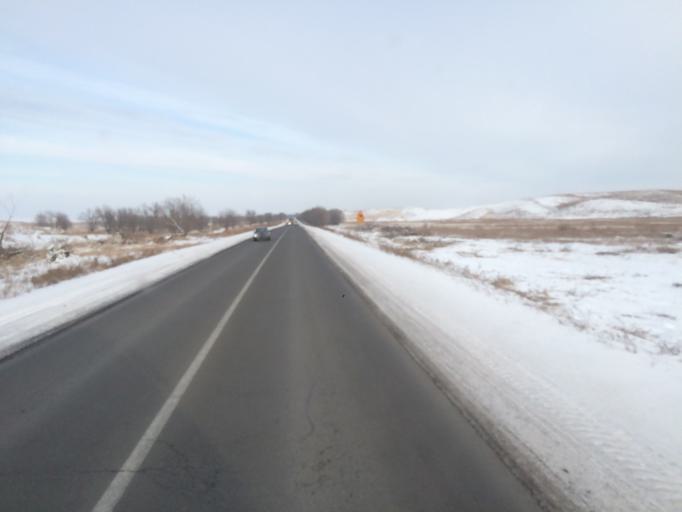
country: KG
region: Chuy
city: Bystrovka
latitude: 43.3237
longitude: 75.8114
